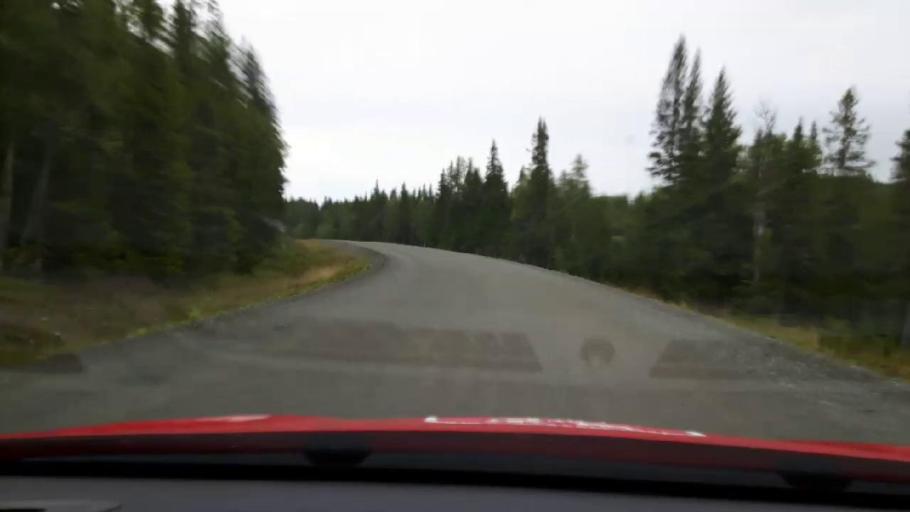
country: SE
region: Jaemtland
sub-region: Are Kommun
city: Are
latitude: 63.4230
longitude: 12.7429
